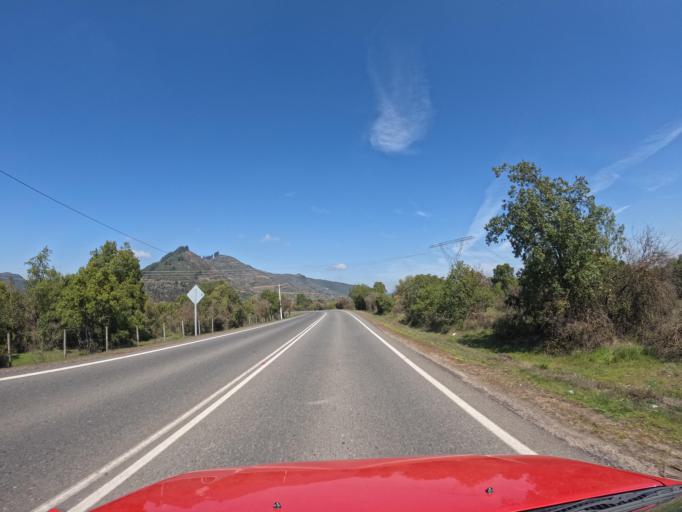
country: CL
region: Maule
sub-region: Provincia de Talca
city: San Clemente
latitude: -35.4772
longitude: -71.2703
